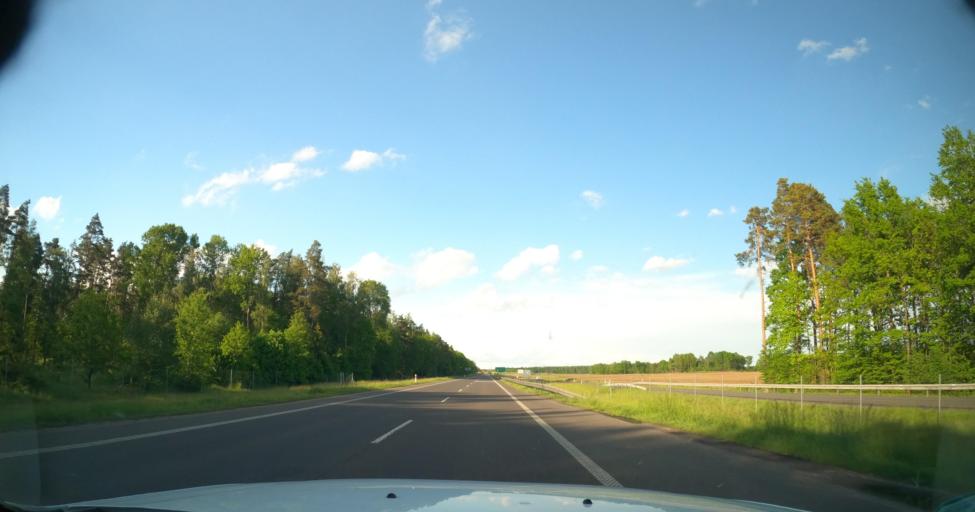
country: PL
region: Warmian-Masurian Voivodeship
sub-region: Powiat braniewski
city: Braniewo
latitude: 54.2830
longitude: 19.7820
